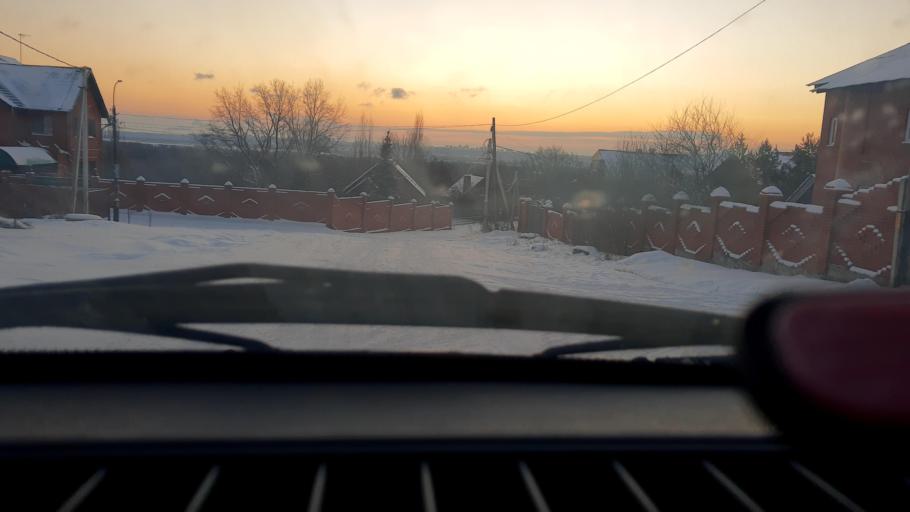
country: RU
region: Bashkortostan
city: Mikhaylovka
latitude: 54.8151
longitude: 55.8982
